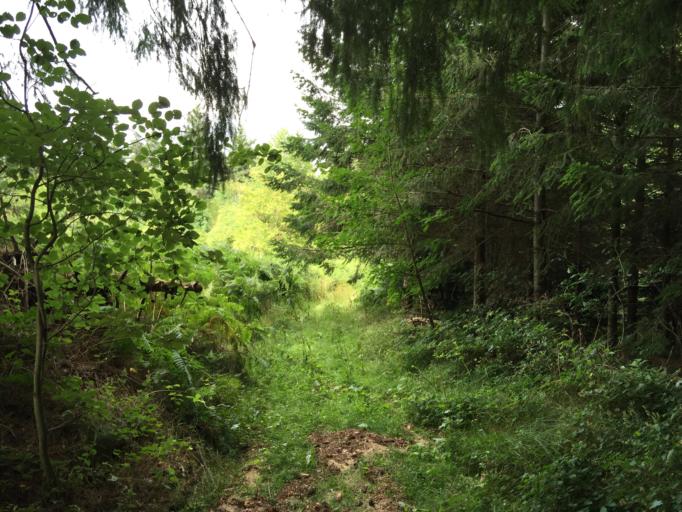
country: FR
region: Rhone-Alpes
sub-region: Departement de la Loire
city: Saint-Bonnet-le-Chateau
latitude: 45.3893
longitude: 4.0407
